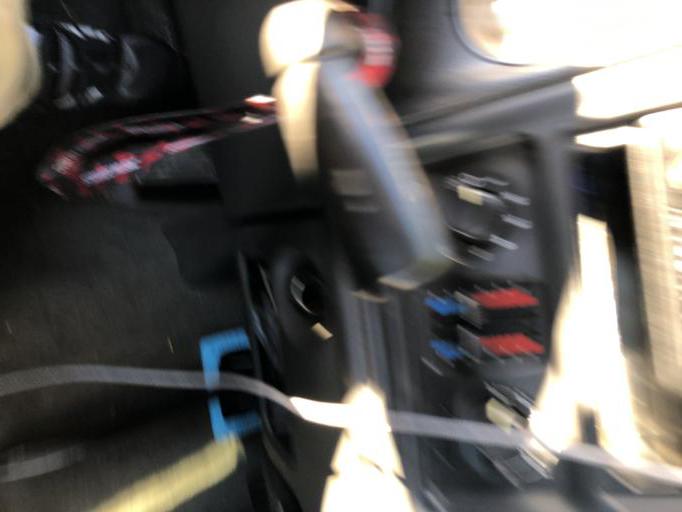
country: US
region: California
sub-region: Sacramento County
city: Foothill Farms
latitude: 38.6562
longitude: -121.3182
